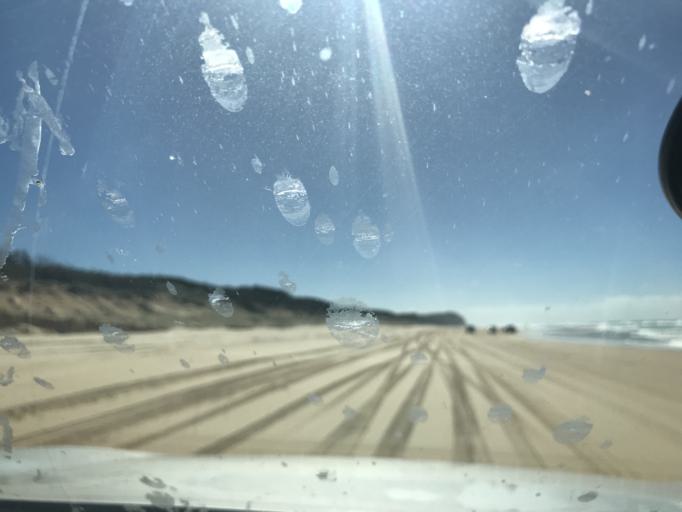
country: AU
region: Queensland
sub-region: Fraser Coast
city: Urangan
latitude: -25.0258
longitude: 153.3534
